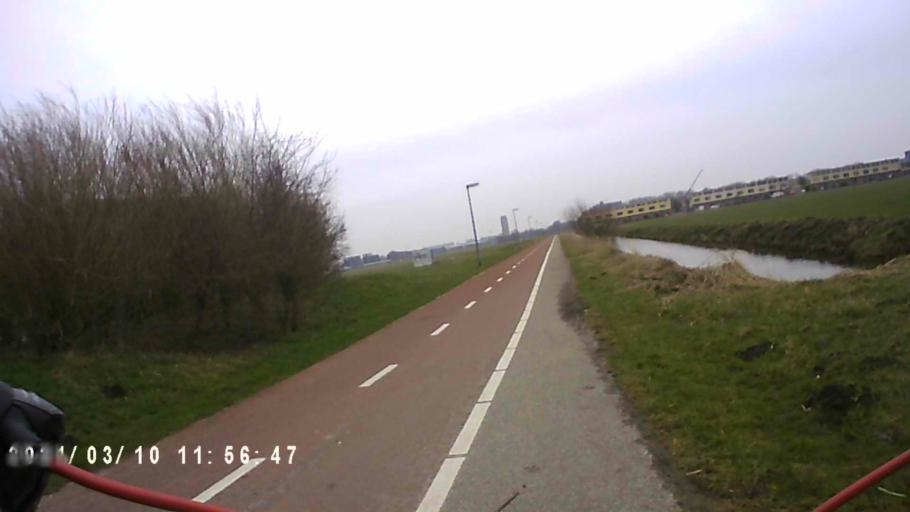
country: NL
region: Groningen
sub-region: Gemeente Zuidhorn
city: Aduard
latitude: 53.2302
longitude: 6.5059
